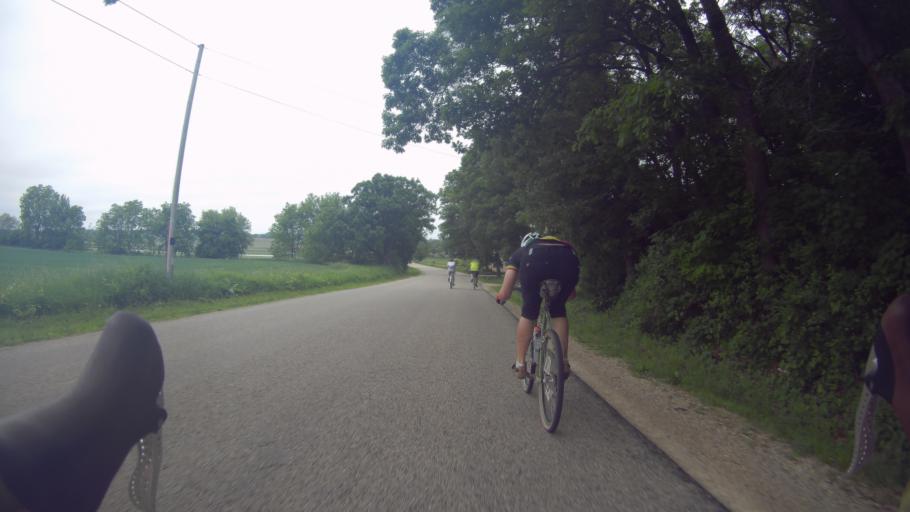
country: US
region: Wisconsin
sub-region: Green County
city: Brooklyn
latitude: 42.8664
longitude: -89.4128
